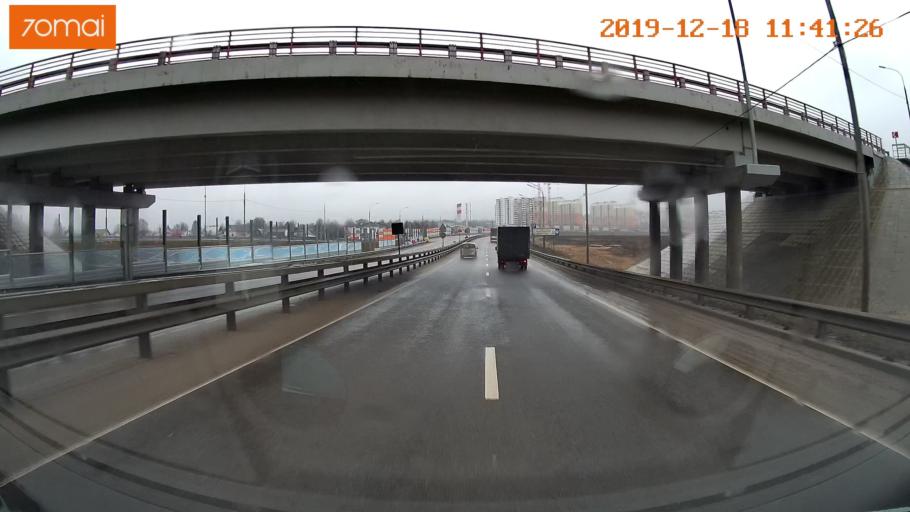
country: RU
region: Moskovskaya
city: Zvenigorod
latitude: 55.7137
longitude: 36.8724
